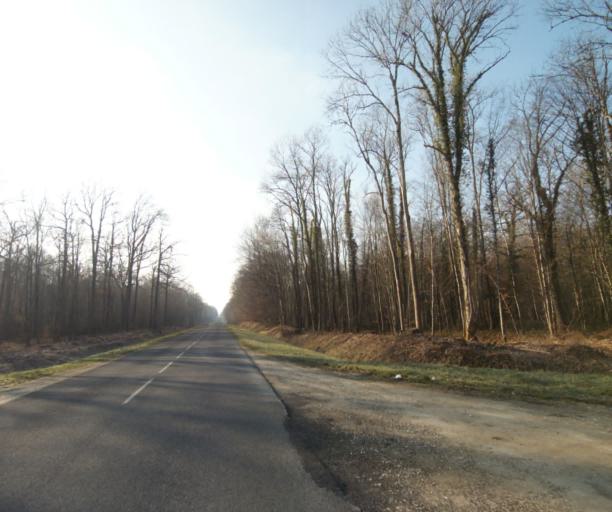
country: FR
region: Champagne-Ardenne
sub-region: Departement de la Haute-Marne
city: Wassy
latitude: 48.4758
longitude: 4.9270
